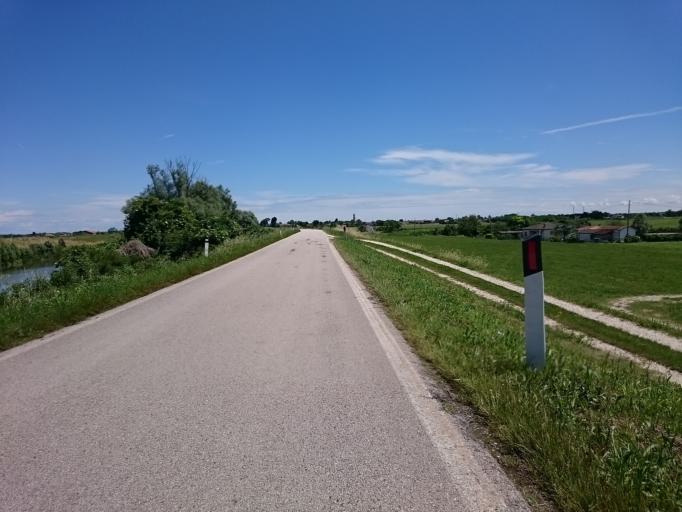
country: IT
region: Veneto
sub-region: Provincia di Padova
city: Correzzola
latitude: 45.2424
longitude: 12.0481
